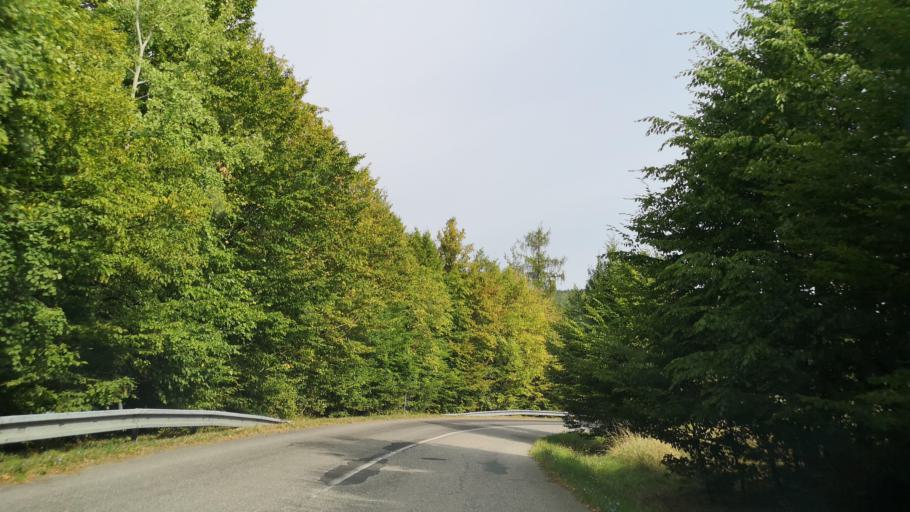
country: SK
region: Banskobystricky
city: Revuca
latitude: 48.5823
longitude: 20.0720
